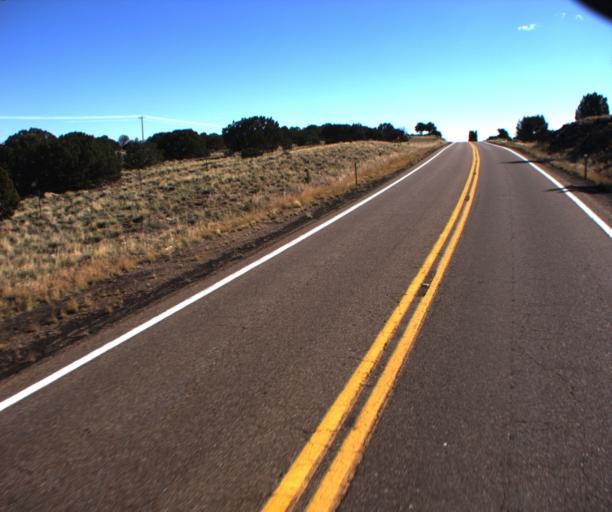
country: US
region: Arizona
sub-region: Apache County
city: Saint Johns
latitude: 34.4827
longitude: -109.5667
